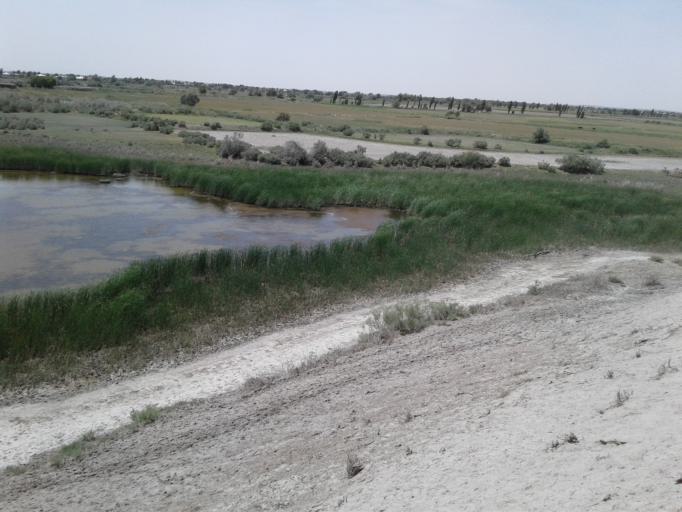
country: TM
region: Dasoguz
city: Tagta
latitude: 41.5410
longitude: 59.9989
